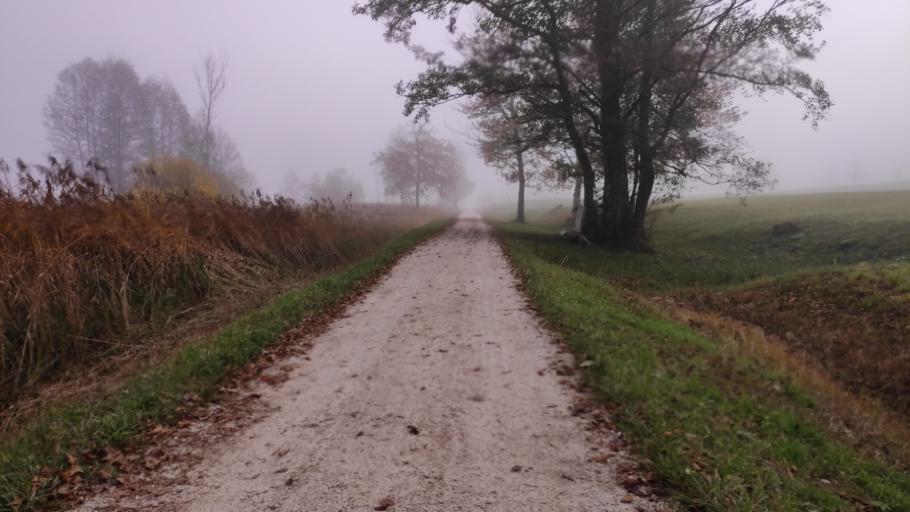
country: AT
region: Upper Austria
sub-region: Politischer Bezirk Gmunden
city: Sankt Wolfgang im Salzkammergut
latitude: 47.7199
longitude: 13.4409
